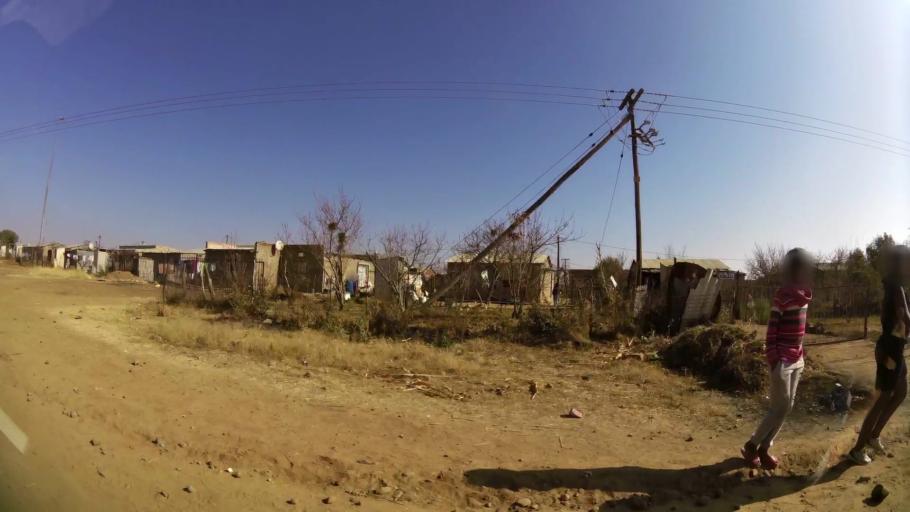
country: ZA
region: Orange Free State
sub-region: Mangaung Metropolitan Municipality
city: Bloemfontein
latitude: -29.1833
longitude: 26.2851
